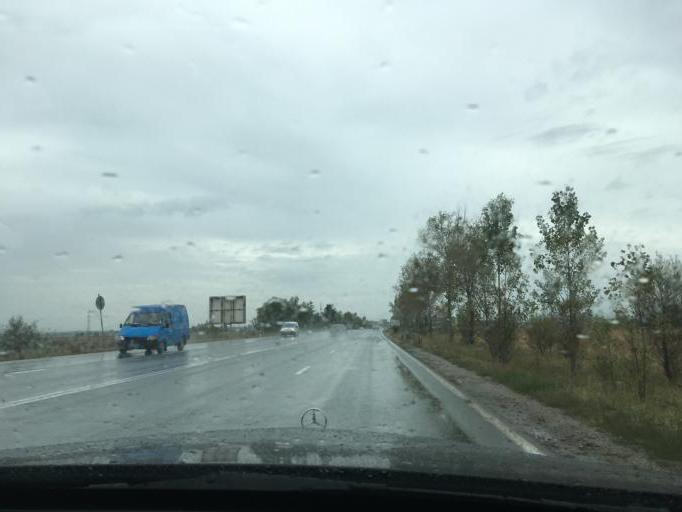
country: BG
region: Sofiya
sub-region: Obshtina Bozhurishte
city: Bozhurishte
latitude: 42.7826
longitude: 23.1688
